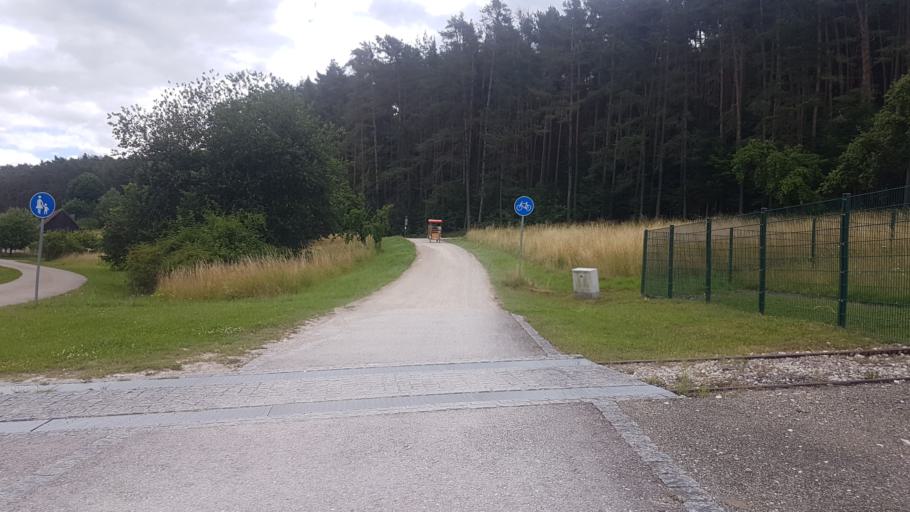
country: DE
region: Bavaria
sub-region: Regierungsbezirk Mittelfranken
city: Pleinfeld
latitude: 49.1192
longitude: 10.9437
